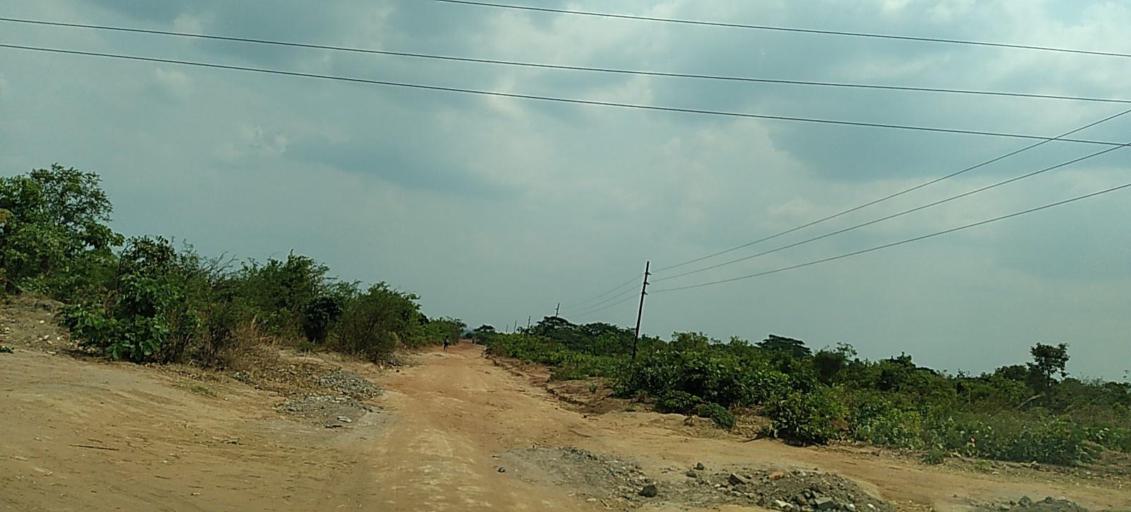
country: ZM
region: Copperbelt
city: Kalulushi
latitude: -12.8689
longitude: 28.0778
